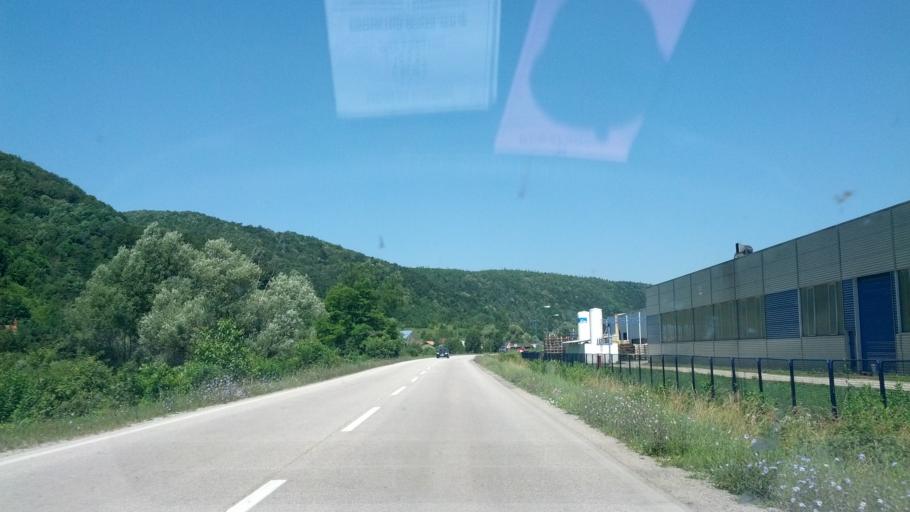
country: BA
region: Federation of Bosnia and Herzegovina
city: Bosanska Krupa
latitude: 44.9074
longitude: 16.1611
